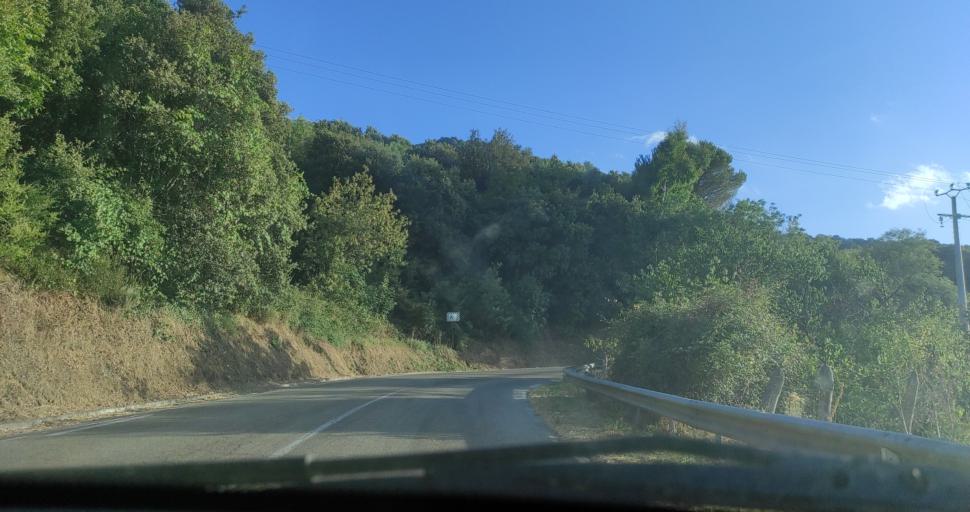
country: FR
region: Corsica
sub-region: Departement de la Corse-du-Sud
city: Appietto
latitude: 42.0310
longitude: 8.7610
